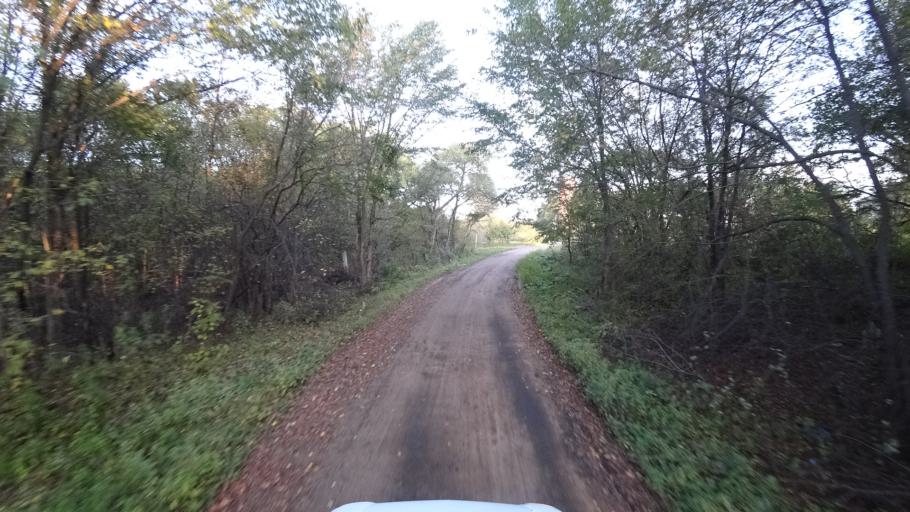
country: RU
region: Amur
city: Arkhara
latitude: 49.3641
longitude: 130.1198
